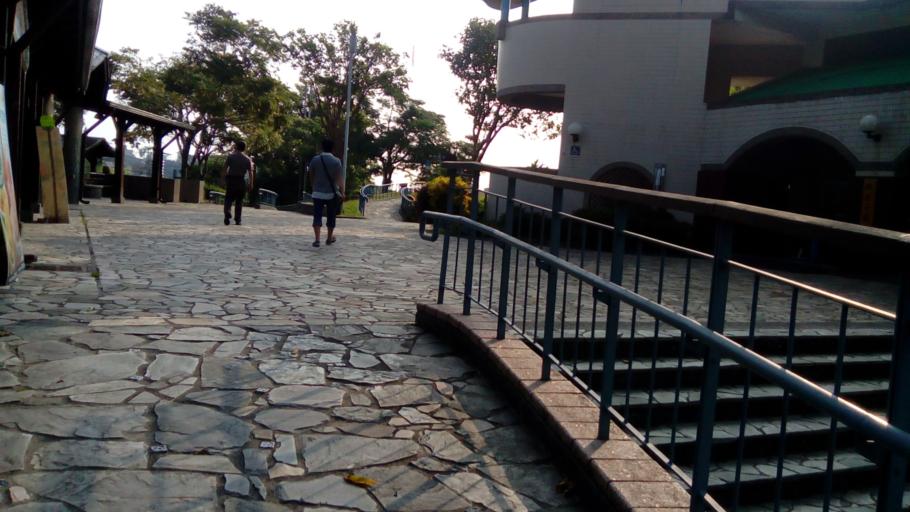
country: TW
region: Taiwan
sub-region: Yilan
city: Yilan
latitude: 24.8309
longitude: 121.7762
